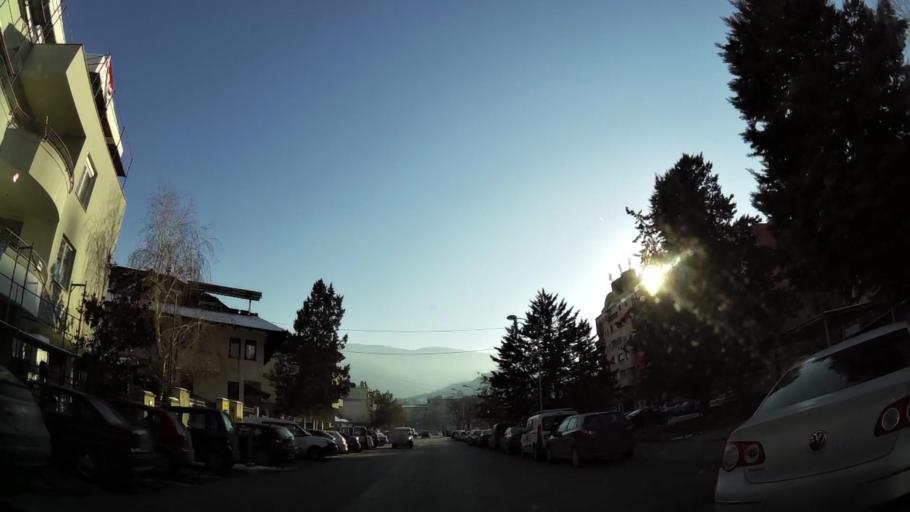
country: MK
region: Karpos
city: Skopje
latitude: 42.0004
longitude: 21.3918
